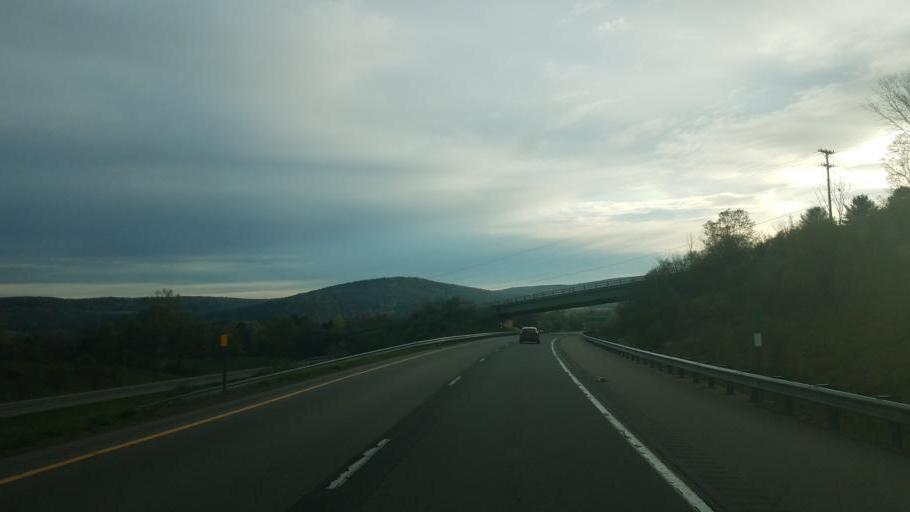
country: US
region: New York
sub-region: Allegany County
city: Belmont
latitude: 42.2979
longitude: -78.0274
